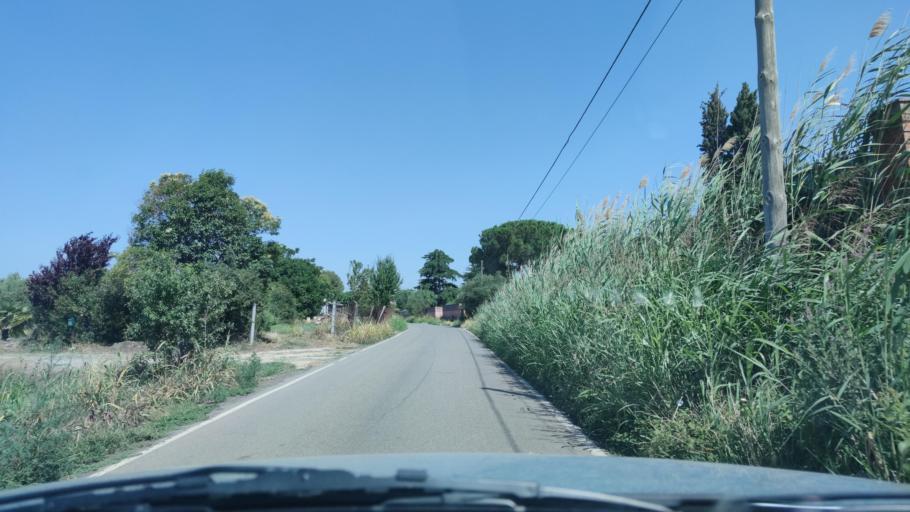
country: ES
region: Catalonia
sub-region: Provincia de Lleida
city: Alpicat
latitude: 41.6469
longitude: 0.5840
